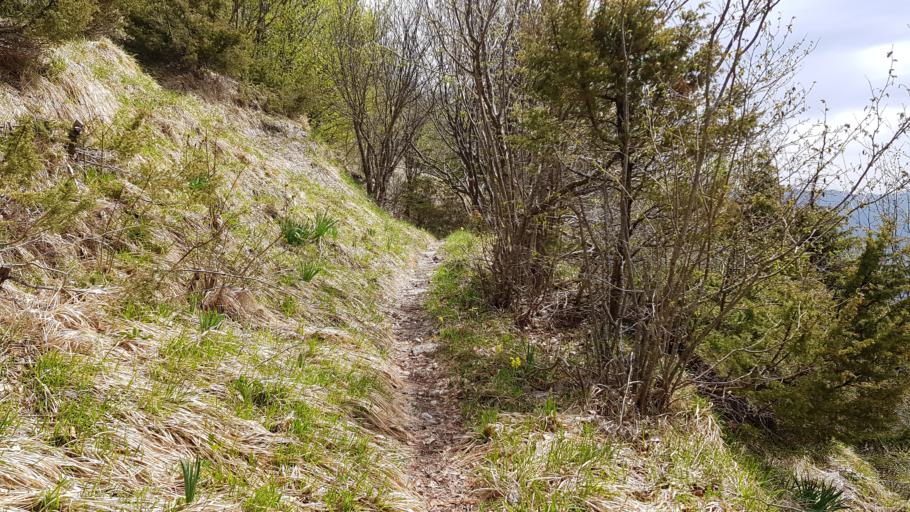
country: IT
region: Liguria
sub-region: Provincia di Genova
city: Gorreto
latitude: 44.6288
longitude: 9.2542
